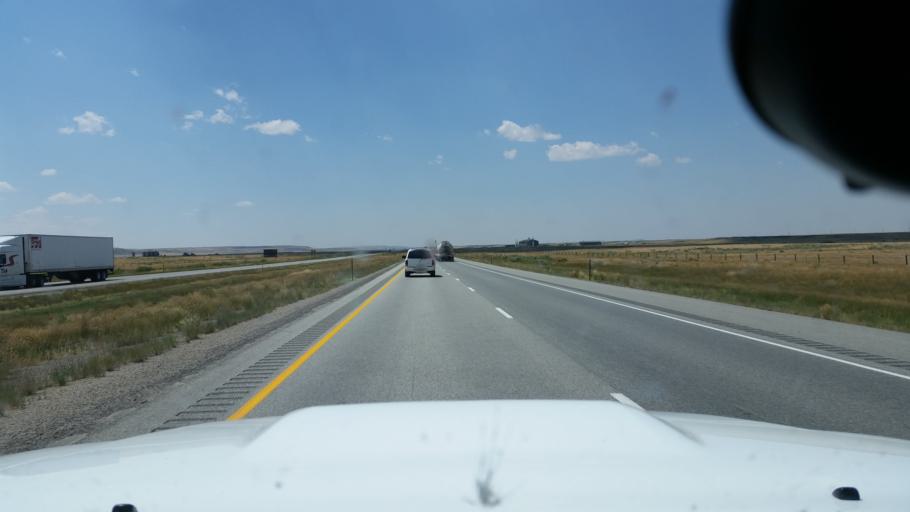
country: US
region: Wyoming
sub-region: Carbon County
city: Rawlins
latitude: 41.6689
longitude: -108.0073
